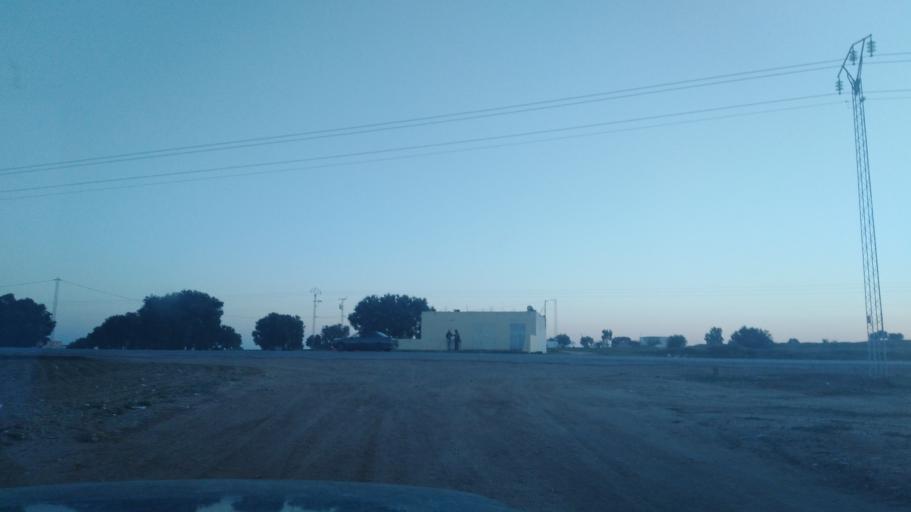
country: TN
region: Safaqis
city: Sfax
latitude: 34.7253
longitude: 10.4473
